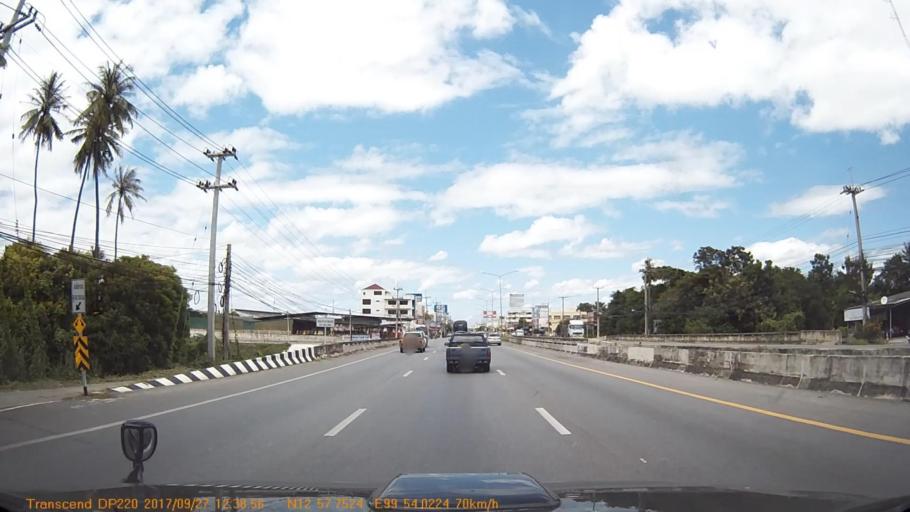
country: TH
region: Phetchaburi
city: Tha Yang
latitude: 12.9627
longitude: 99.9004
